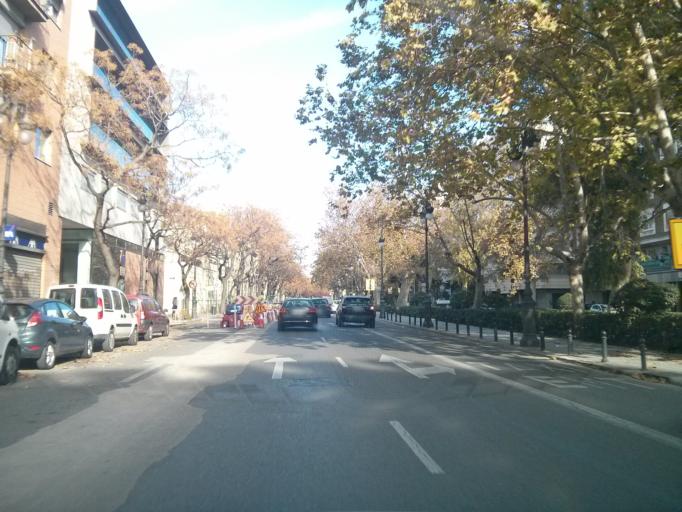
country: ES
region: Valencia
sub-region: Provincia de Valencia
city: Valencia
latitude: 39.4764
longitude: -0.3840
